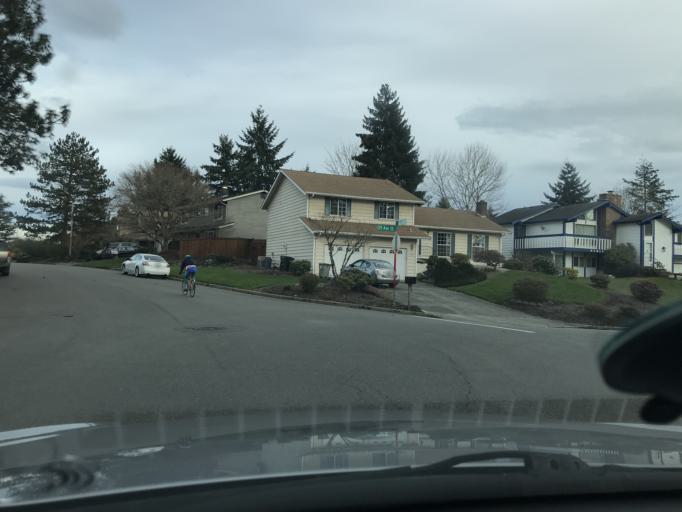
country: US
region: Washington
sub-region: King County
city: East Hill-Meridian
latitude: 47.4112
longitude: -122.1748
